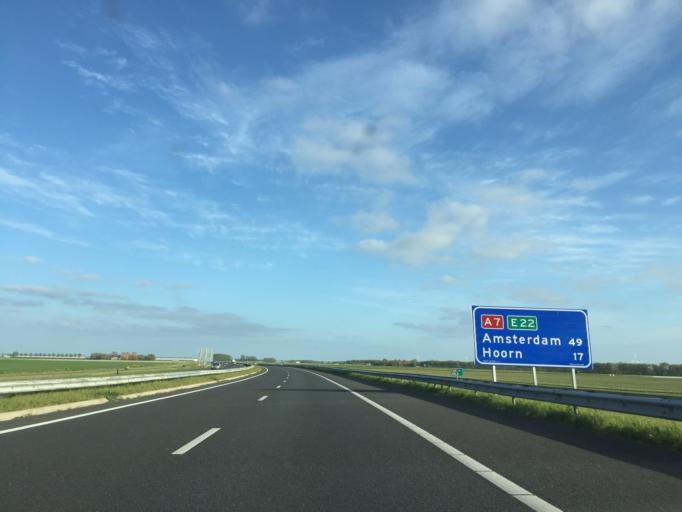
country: NL
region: North Holland
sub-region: Gemeente Medemblik
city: Opperdoes
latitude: 52.8008
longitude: 5.0114
